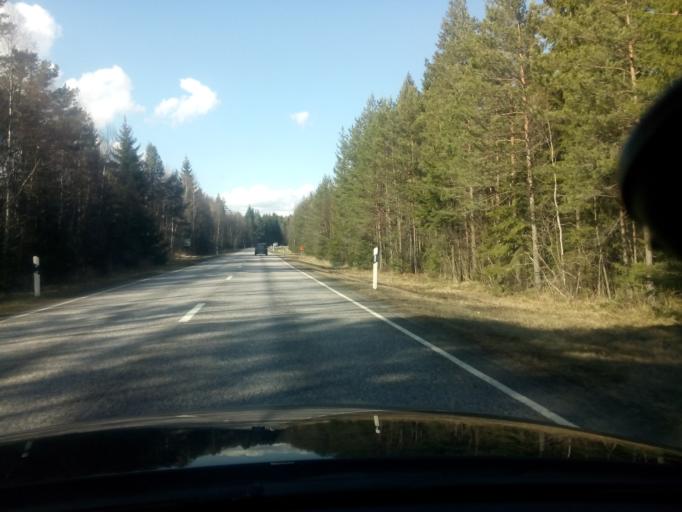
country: SE
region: Soedermanland
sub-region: Flens Kommun
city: Malmkoping
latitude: 59.1994
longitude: 16.7891
